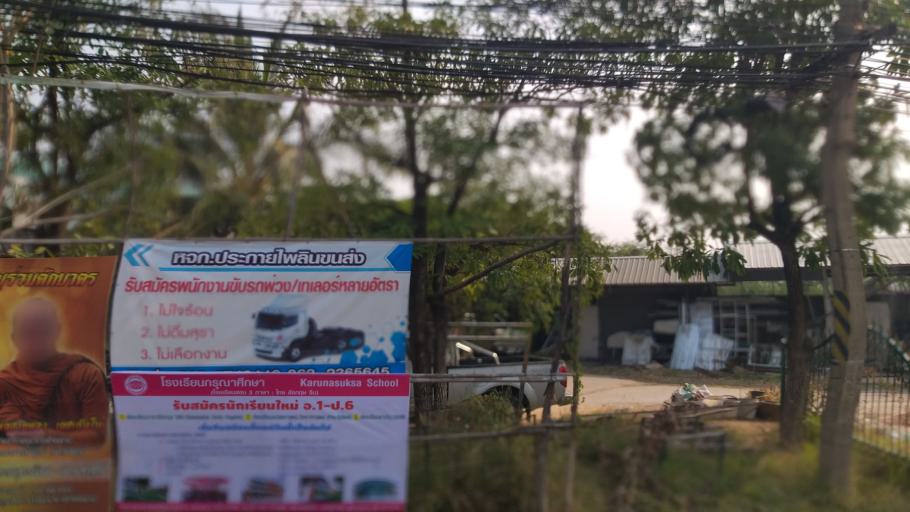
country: TH
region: Khon Kaen
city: Ban Phai
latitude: 16.0687
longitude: 102.7208
